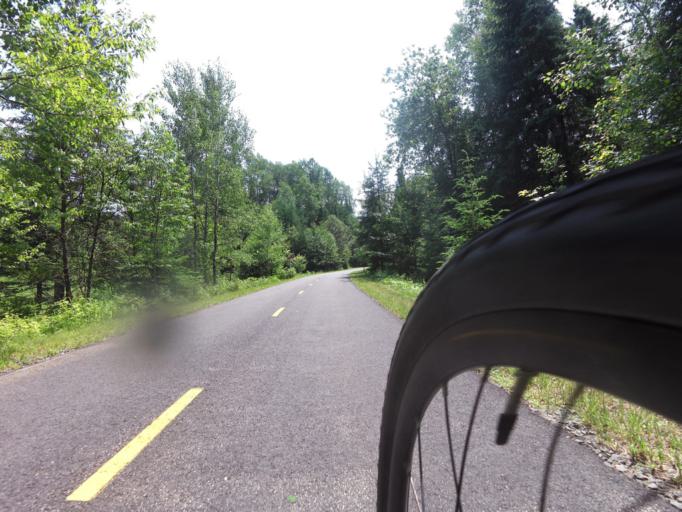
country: CA
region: Quebec
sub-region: Laurentides
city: Mont-Tremblant
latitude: 46.1532
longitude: -74.5952
